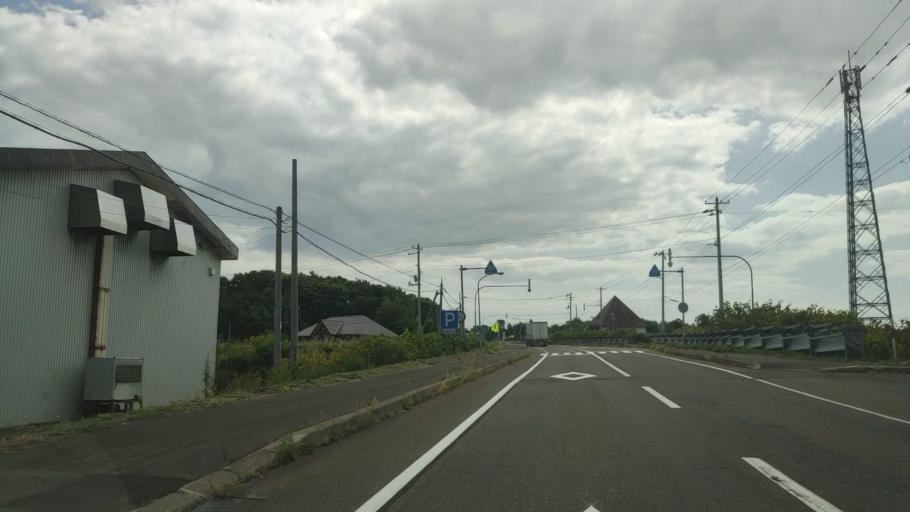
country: JP
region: Hokkaido
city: Rumoi
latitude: 44.5659
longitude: 141.7863
